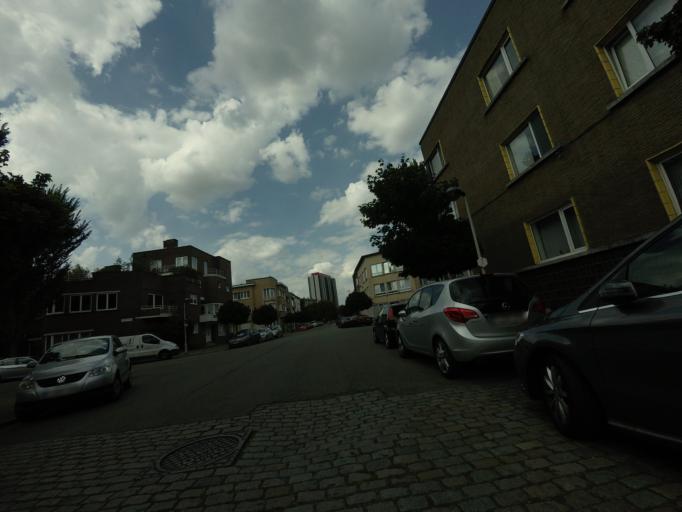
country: BE
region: Flanders
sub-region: Provincie Antwerpen
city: Antwerpen
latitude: 51.1917
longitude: 4.3912
